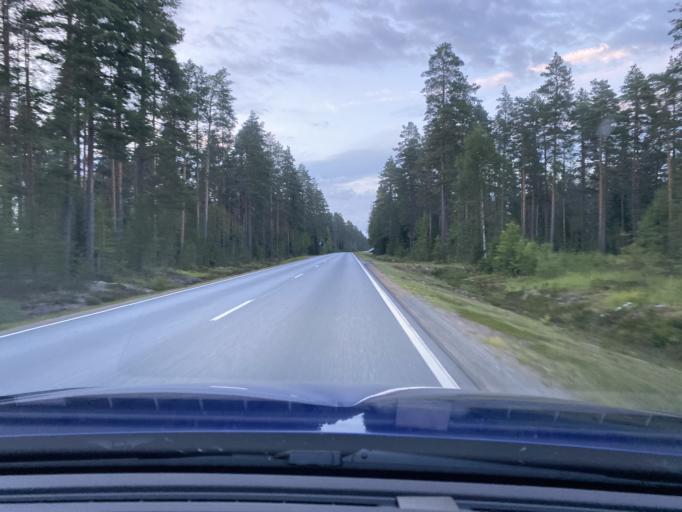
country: FI
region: Satakunta
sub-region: Pohjois-Satakunta
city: Honkajoki
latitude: 62.1339
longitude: 22.2496
